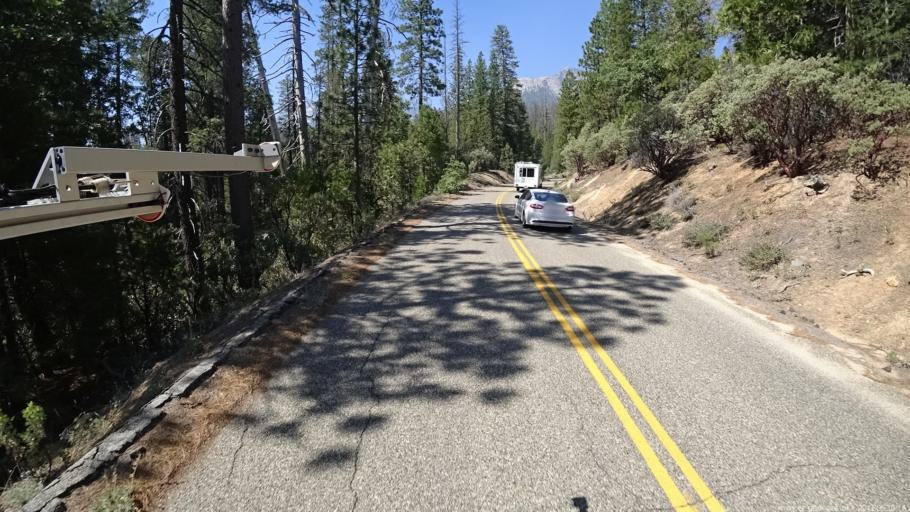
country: US
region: California
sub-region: Madera County
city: Oakhurst
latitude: 37.3731
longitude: -119.3904
